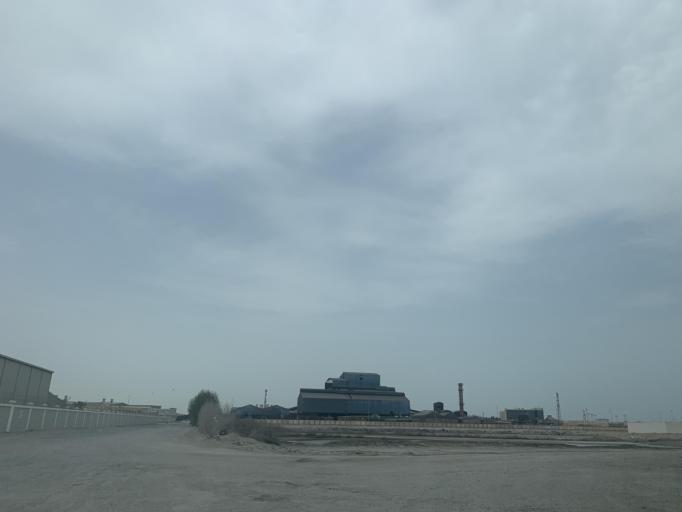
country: BH
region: Muharraq
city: Al Hadd
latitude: 26.2049
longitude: 50.6708
